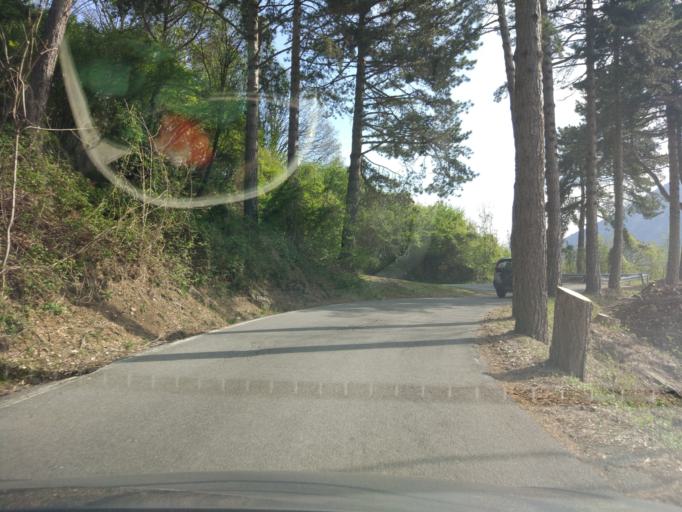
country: IT
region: Lombardy
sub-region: Provincia di Lecco
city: Ballabio
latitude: 45.8966
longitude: 9.4098
